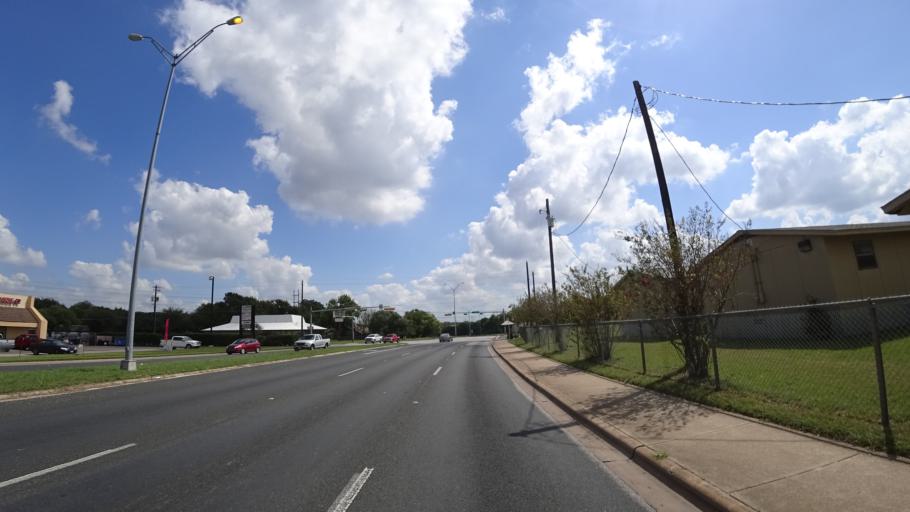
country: US
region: Texas
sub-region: Travis County
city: Onion Creek
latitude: 30.1960
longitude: -97.7857
